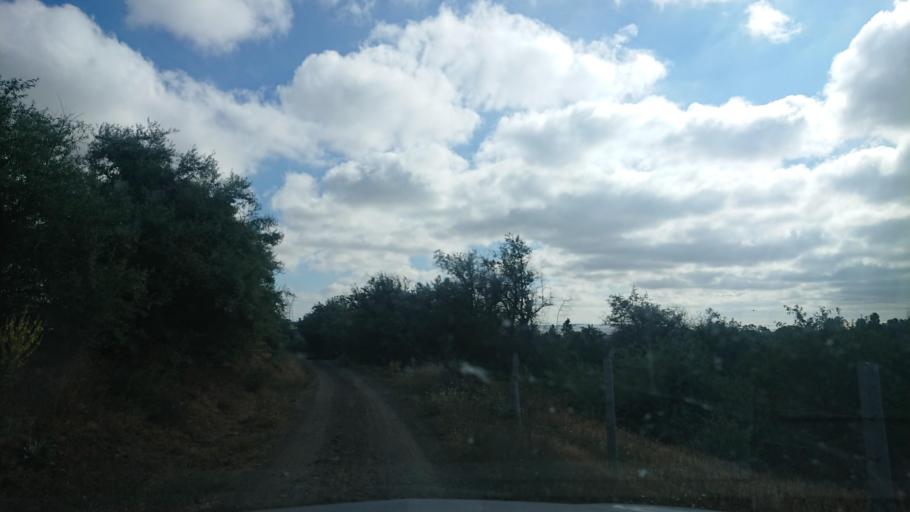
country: TR
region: Aksaray
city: Agacoren
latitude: 38.8596
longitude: 33.9390
